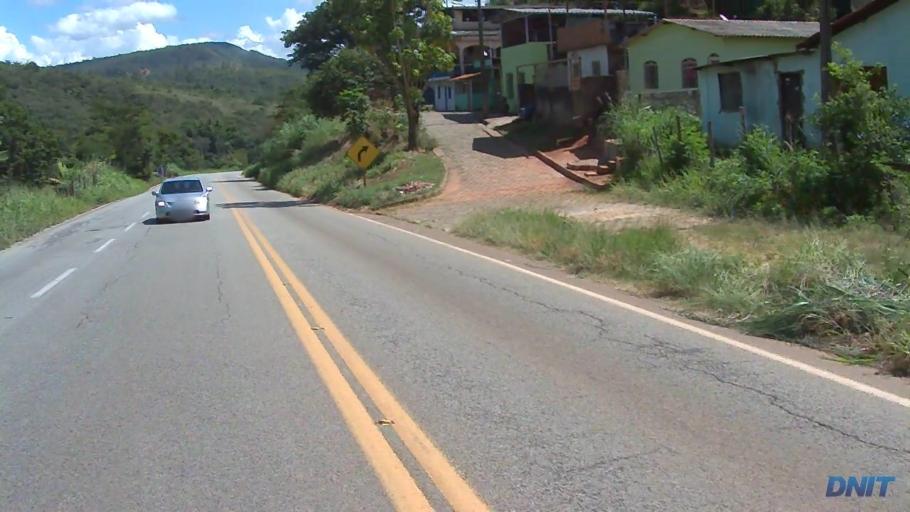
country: BR
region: Minas Gerais
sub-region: Nova Era
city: Nova Era
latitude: -19.8189
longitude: -43.0678
